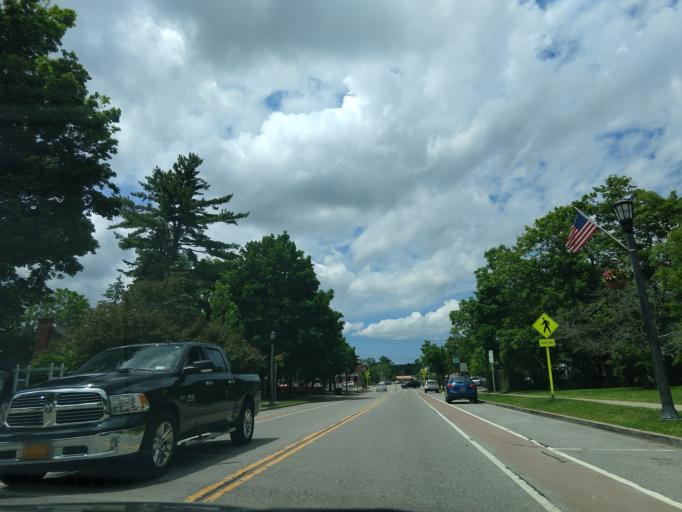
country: US
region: New York
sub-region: Erie County
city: East Aurora
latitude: 42.7680
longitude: -78.6245
